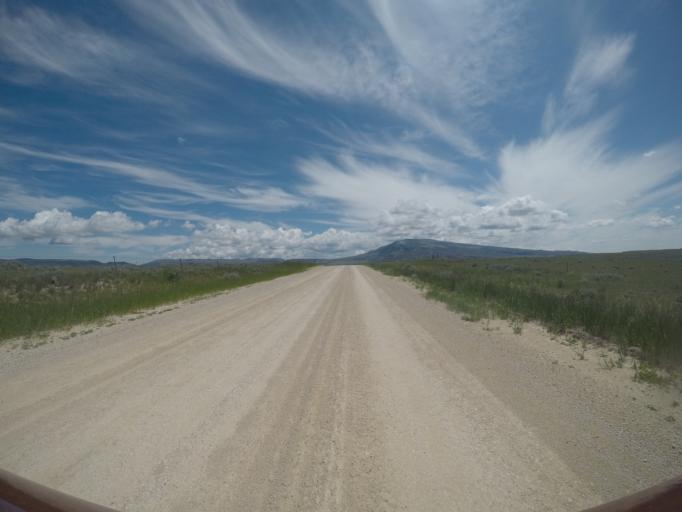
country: US
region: Wyoming
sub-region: Park County
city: Powell
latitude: 45.2050
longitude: -108.7413
